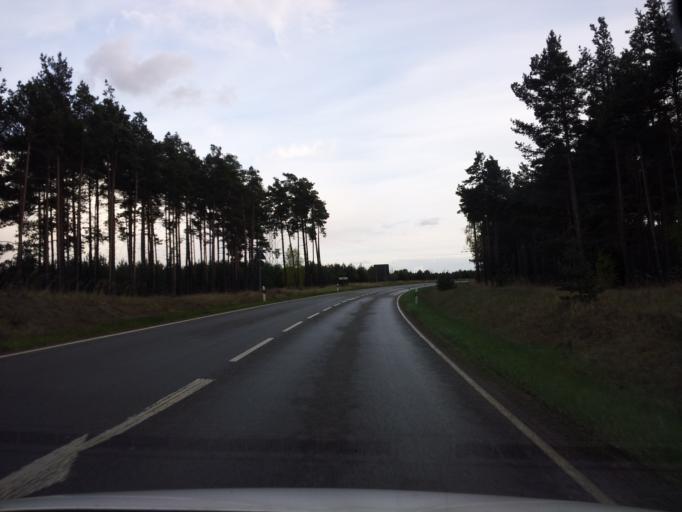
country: DE
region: Brandenburg
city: Heinersbruck
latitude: 51.8291
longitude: 14.5211
